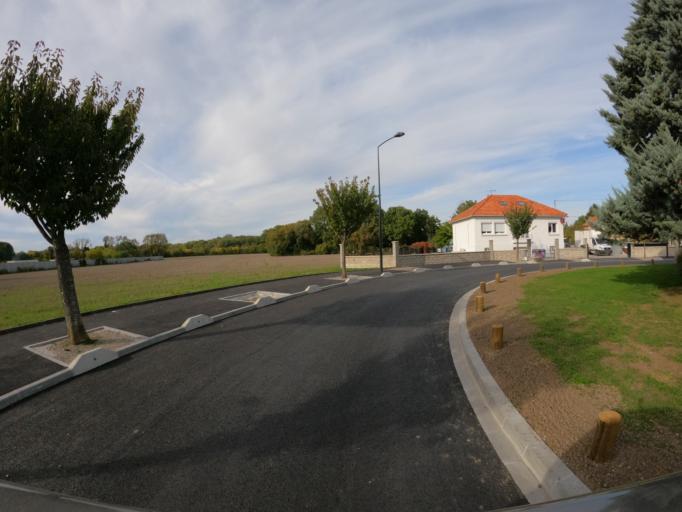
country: FR
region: Ile-de-France
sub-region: Departement de Seine-et-Marne
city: Pontault-Combault
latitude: 48.7935
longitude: 2.5995
